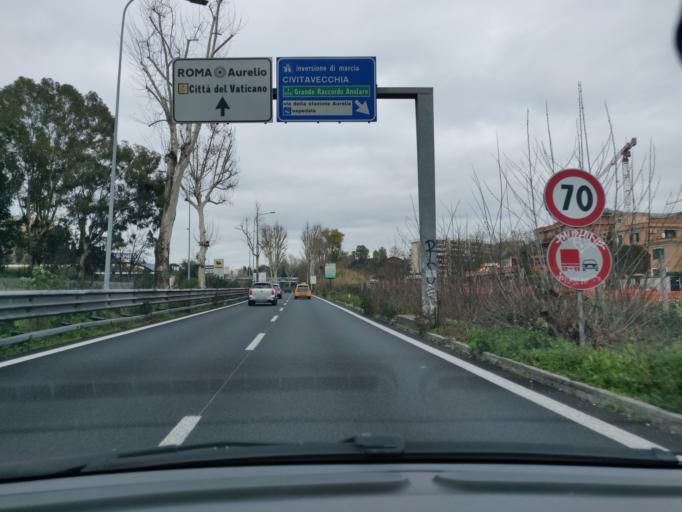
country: IT
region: Latium
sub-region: Citta metropolitana di Roma Capitale
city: La Massimina-Casal Lumbroso
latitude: 41.8855
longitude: 12.4000
